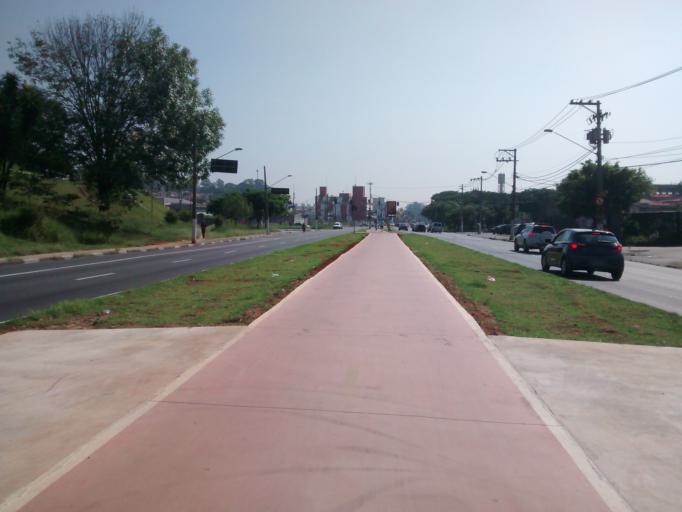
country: BR
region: Sao Paulo
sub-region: Taboao Da Serra
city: Taboao da Serra
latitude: -23.5916
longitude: -46.7391
